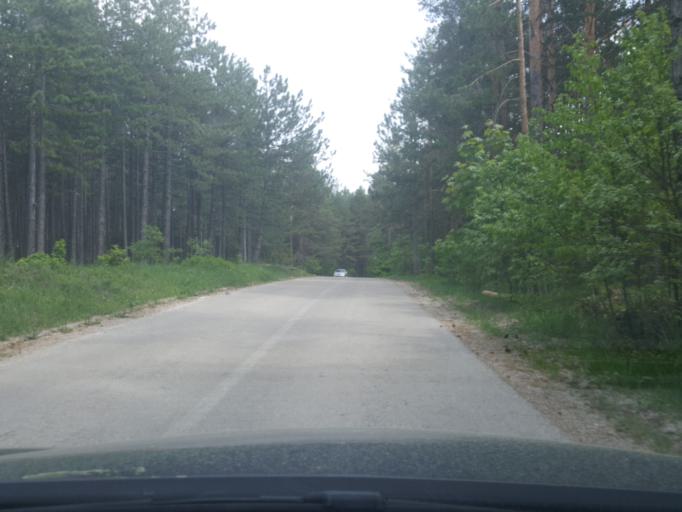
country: RS
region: Central Serbia
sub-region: Zlatiborski Okrug
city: Bajina Basta
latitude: 43.8895
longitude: 19.5341
